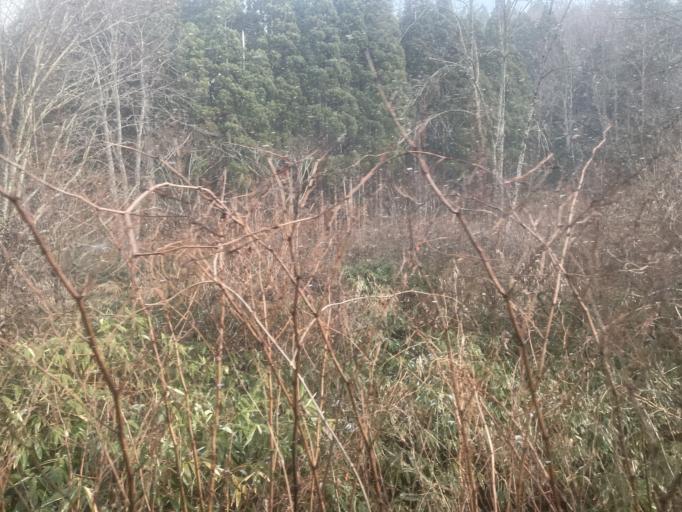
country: JP
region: Aomori
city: Goshogawara
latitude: 41.0846
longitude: 140.5222
